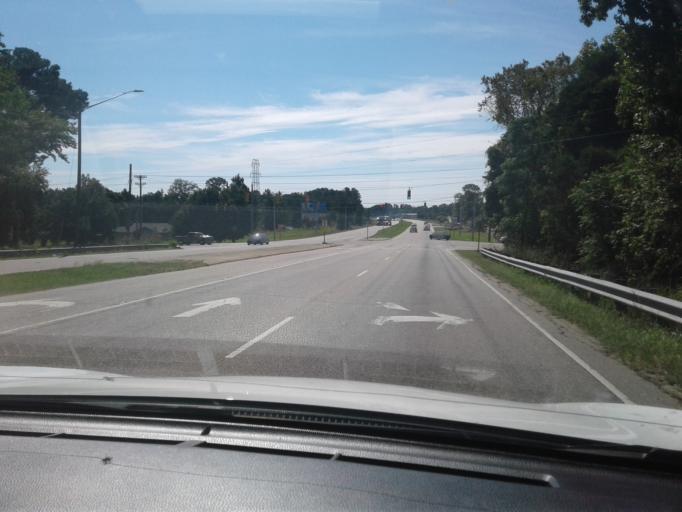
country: US
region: North Carolina
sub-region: Harnett County
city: Erwin
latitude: 35.3288
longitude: -78.6612
